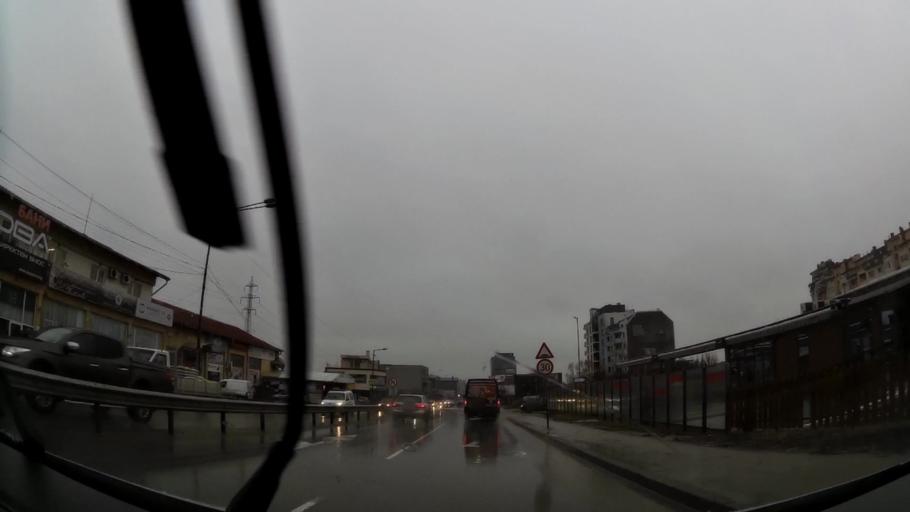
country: BG
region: Sofia-Capital
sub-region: Stolichna Obshtina
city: Sofia
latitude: 42.6375
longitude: 23.3343
